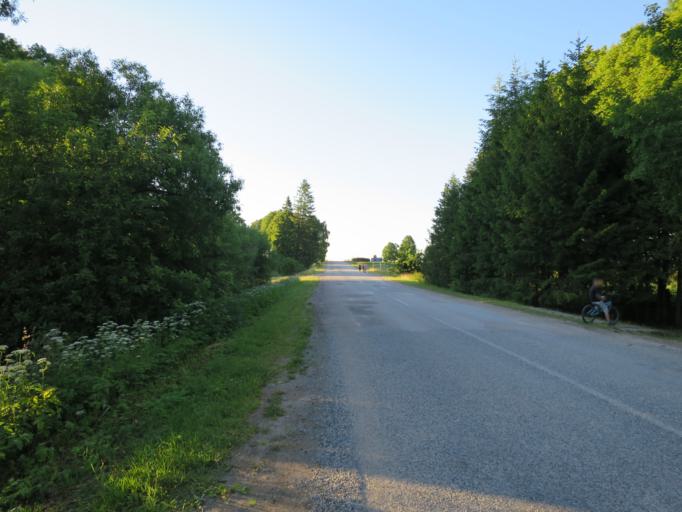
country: LV
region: Rucavas
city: Rucava
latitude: 56.3327
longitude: 21.3092
